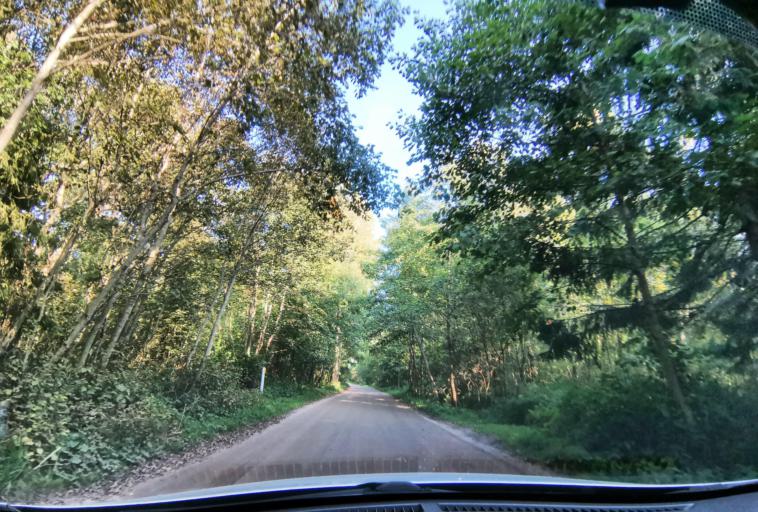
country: LT
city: Nida
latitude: 55.1627
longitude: 20.8226
